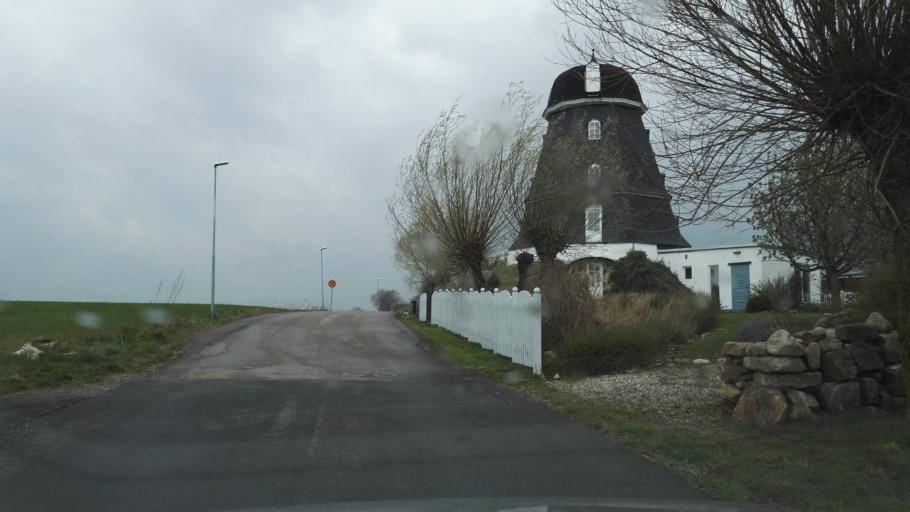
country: SE
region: Skane
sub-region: Simrishamns Kommun
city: Simrishamn
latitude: 55.4840
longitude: 14.2878
